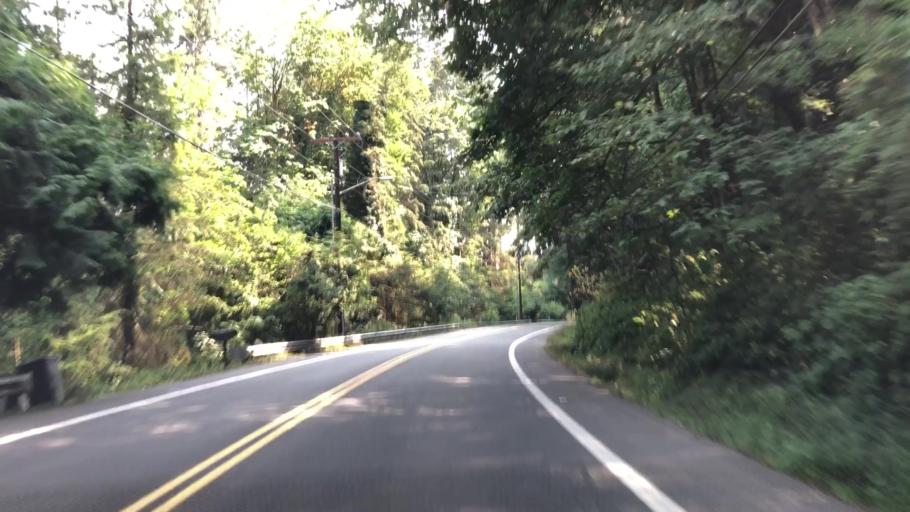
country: US
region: Washington
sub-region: King County
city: Kenmore
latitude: 47.7722
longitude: -122.2488
